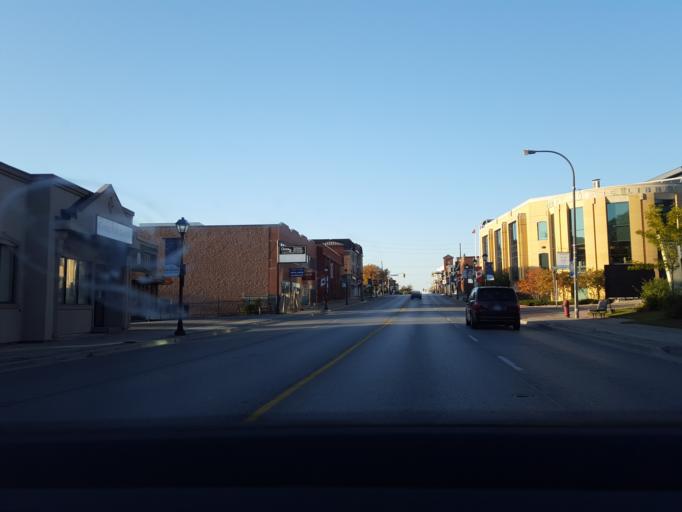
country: CA
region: Ontario
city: Newmarket
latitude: 43.9963
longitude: -79.4667
